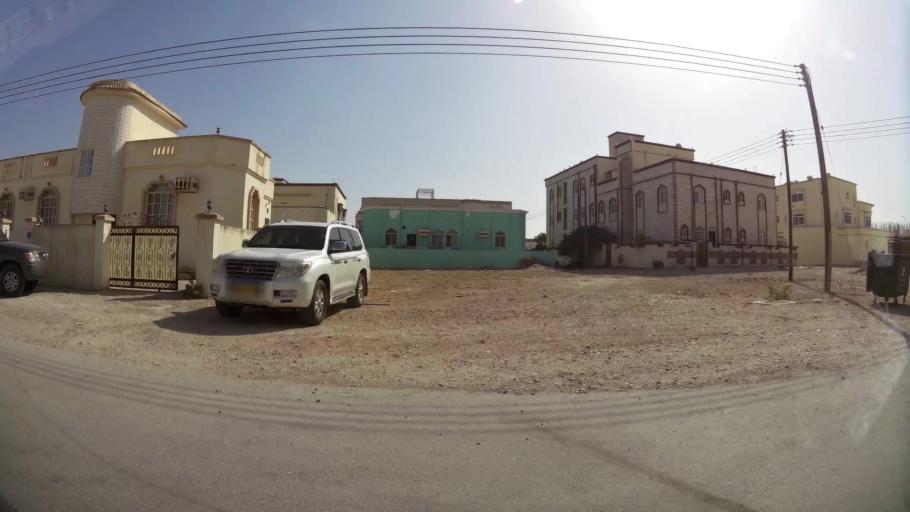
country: OM
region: Zufar
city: Salalah
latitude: 17.0062
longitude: 54.0080
